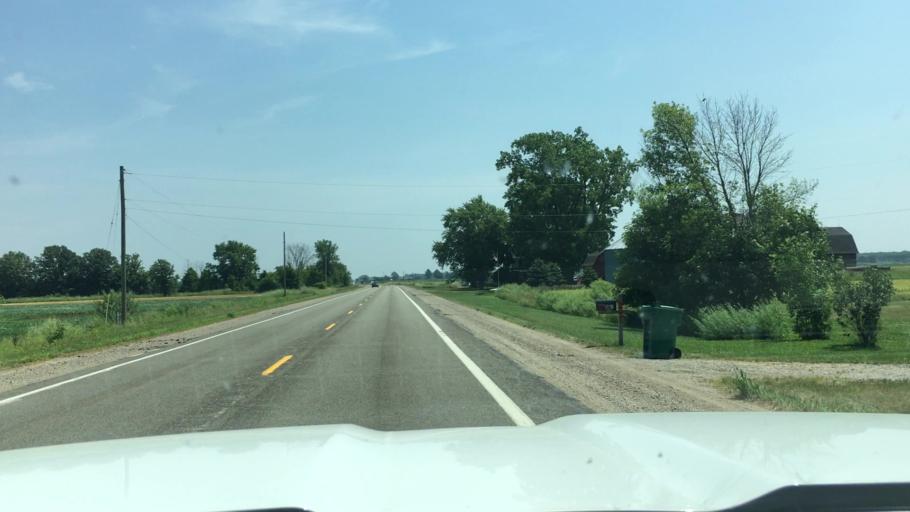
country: US
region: Michigan
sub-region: Gratiot County
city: Ithaca
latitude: 43.1757
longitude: -84.4880
